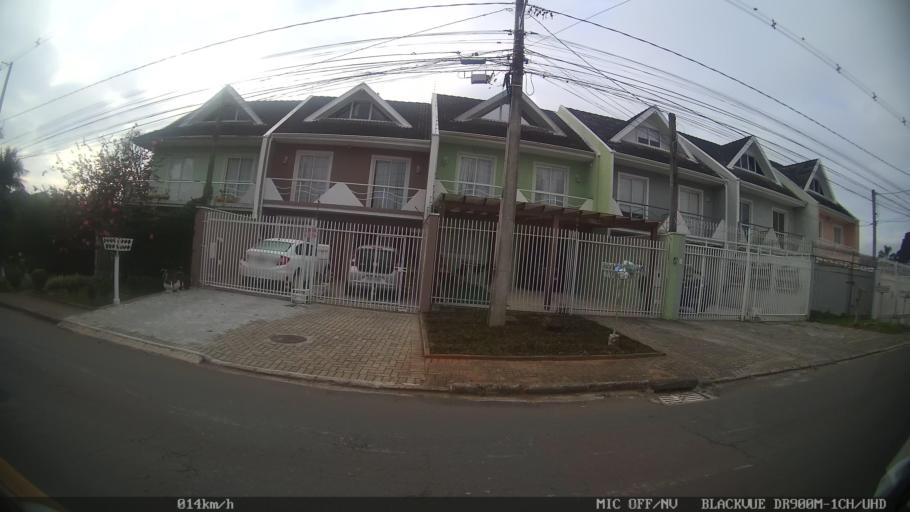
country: BR
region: Parana
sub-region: Almirante Tamandare
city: Almirante Tamandare
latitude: -25.3844
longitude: -49.3363
